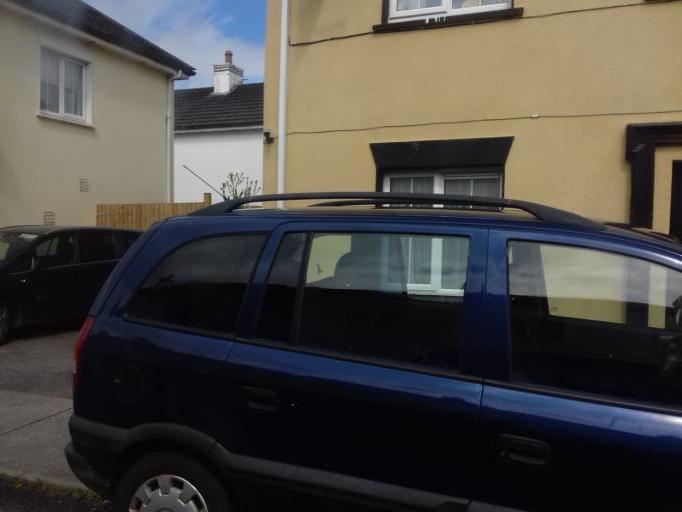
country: IE
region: Leinster
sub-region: Laois
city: Portlaoise
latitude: 53.0476
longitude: -7.3205
